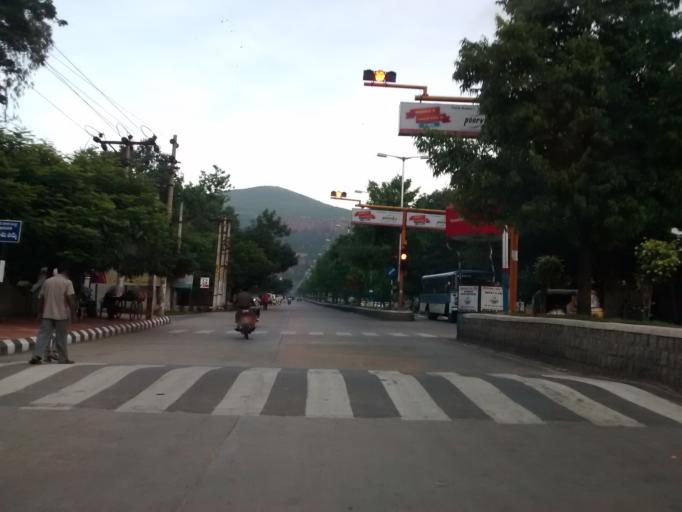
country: IN
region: Andhra Pradesh
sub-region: Chittoor
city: Akkarampalle
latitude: 13.6475
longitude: 79.4263
